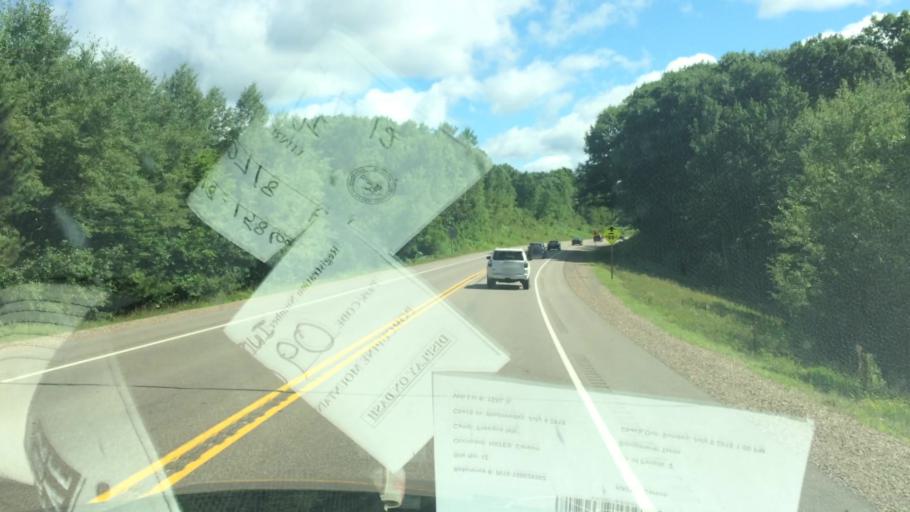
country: US
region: Wisconsin
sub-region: Oneida County
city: Rhinelander
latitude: 45.6080
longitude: -89.5526
